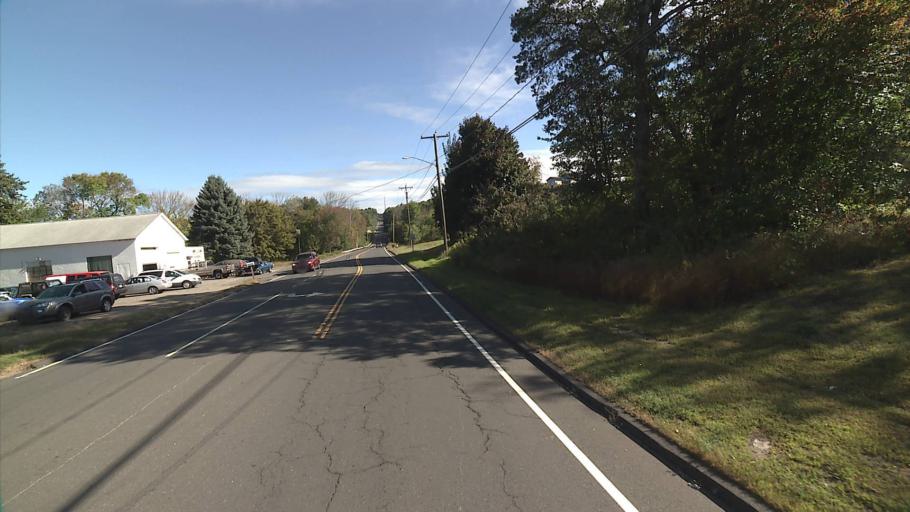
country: US
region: Connecticut
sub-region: New Haven County
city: Wolcott
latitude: 41.6072
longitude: -72.9852
